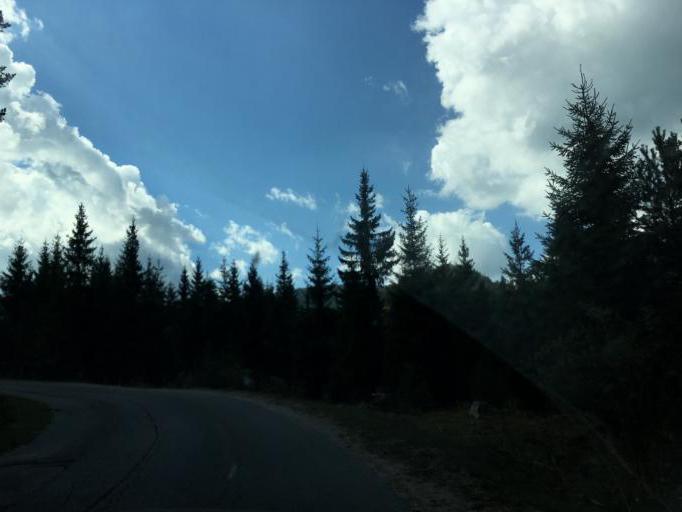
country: BG
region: Pazardzhik
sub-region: Obshtina Batak
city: Batak
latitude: 41.9260
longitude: 24.2812
